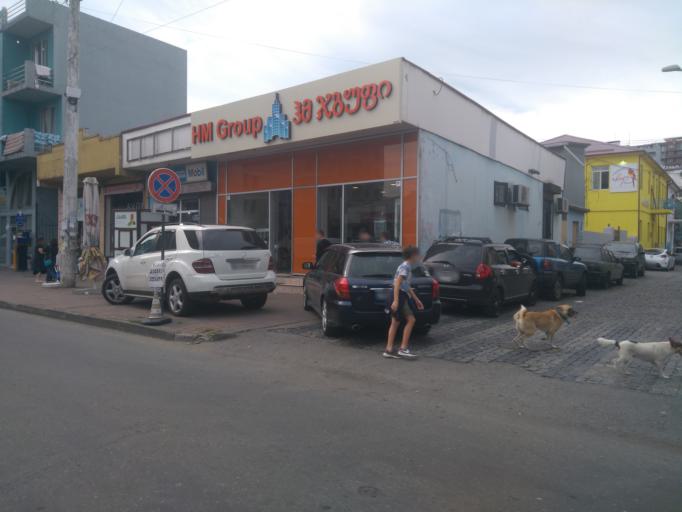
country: GE
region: Ajaria
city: Batumi
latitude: 41.6435
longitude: 41.6317
